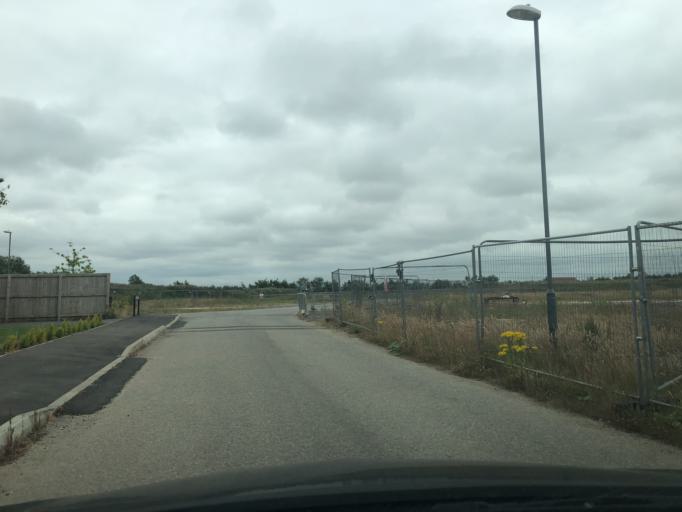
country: GB
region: England
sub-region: North Yorkshire
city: Filey
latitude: 54.2038
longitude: -0.2985
